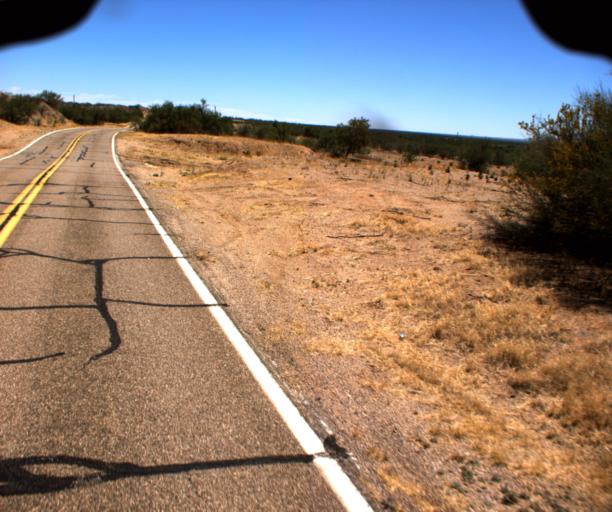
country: US
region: Arizona
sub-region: Pima County
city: Three Points
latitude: 31.9122
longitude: -111.3901
